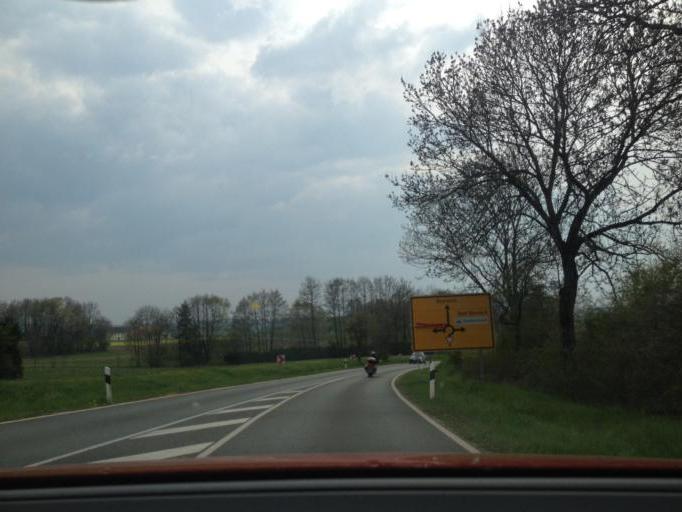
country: DE
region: Bavaria
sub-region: Upper Franconia
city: Goldkronach
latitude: 50.0053
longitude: 11.6835
